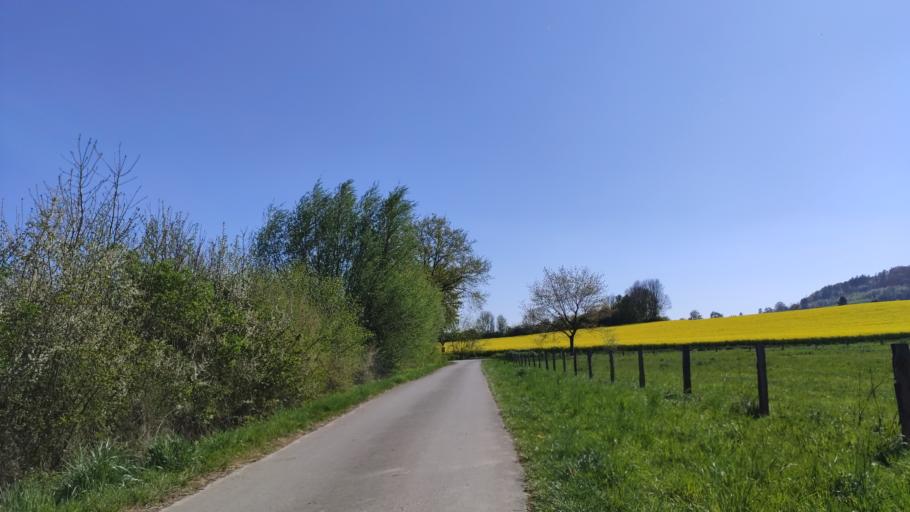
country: DE
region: Lower Saxony
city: Boffzen
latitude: 51.7422
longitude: 9.3603
